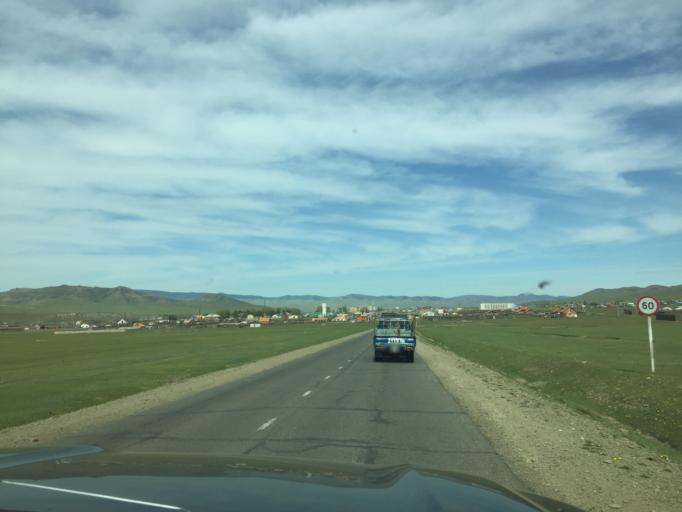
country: MN
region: Central Aimak
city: Ihsueuej
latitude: 48.2180
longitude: 106.3043
